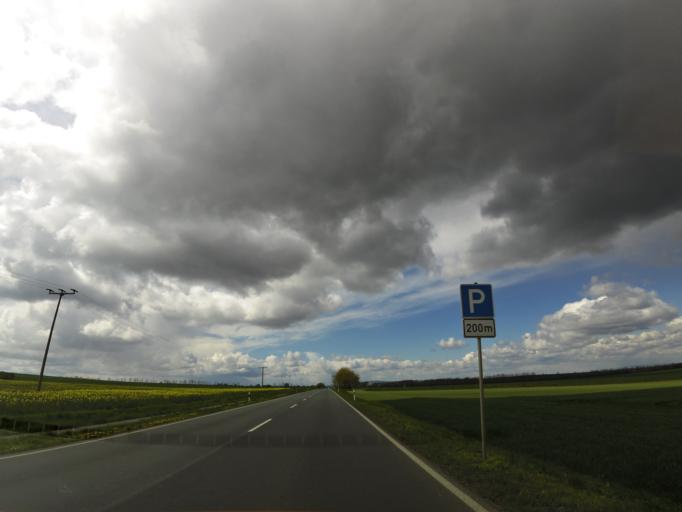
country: DE
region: Saxony-Anhalt
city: Kroppenstedt
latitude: 51.9411
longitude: 11.2791
